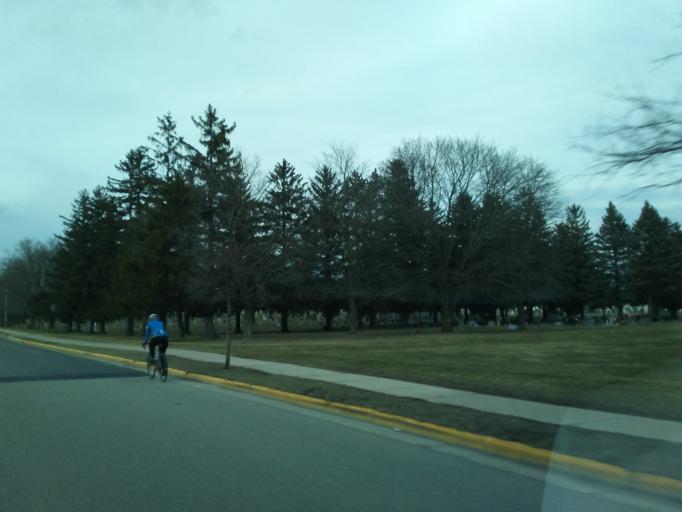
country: US
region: Wisconsin
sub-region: Dane County
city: Verona
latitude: 42.9959
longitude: -89.5336
